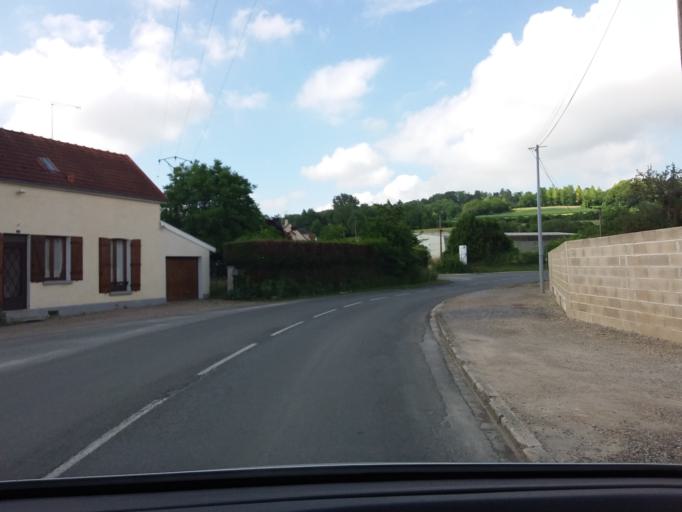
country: FR
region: Champagne-Ardenne
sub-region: Departement de la Marne
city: Fismes
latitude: 49.3792
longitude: 3.7306
